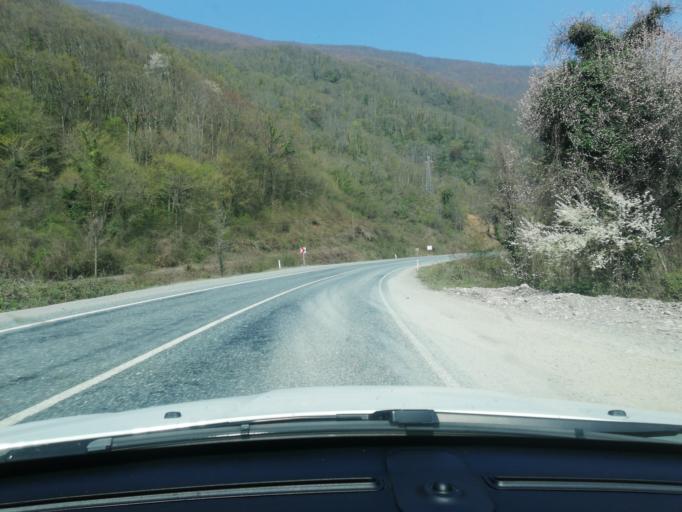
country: TR
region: Zonguldak
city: Gokcebey
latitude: 41.2650
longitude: 32.1585
